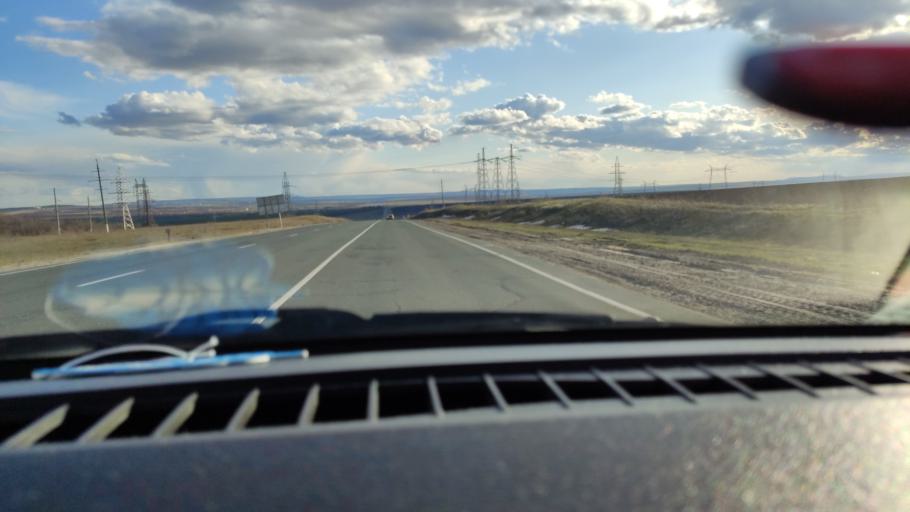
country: RU
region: Saratov
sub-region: Saratovskiy Rayon
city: Saratov
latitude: 51.7655
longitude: 46.0772
